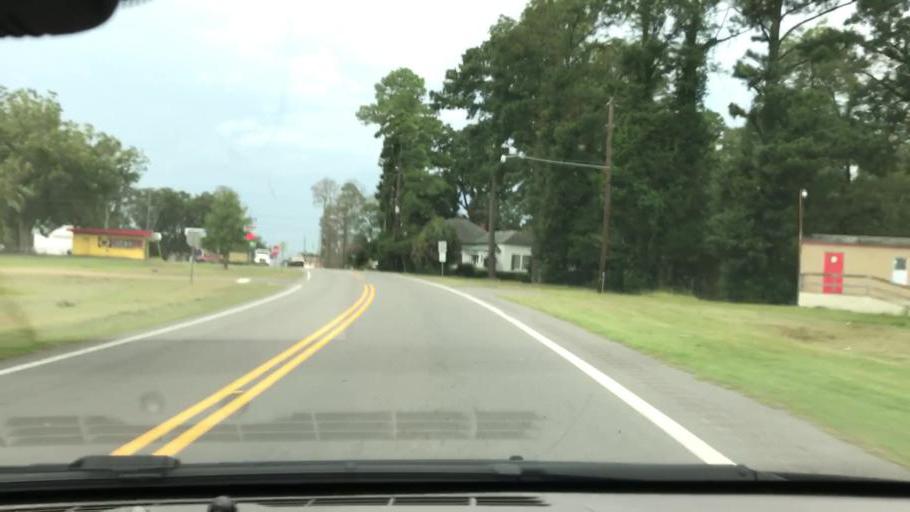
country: US
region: Alabama
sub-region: Houston County
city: Ashford
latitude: 31.2920
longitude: -85.1066
